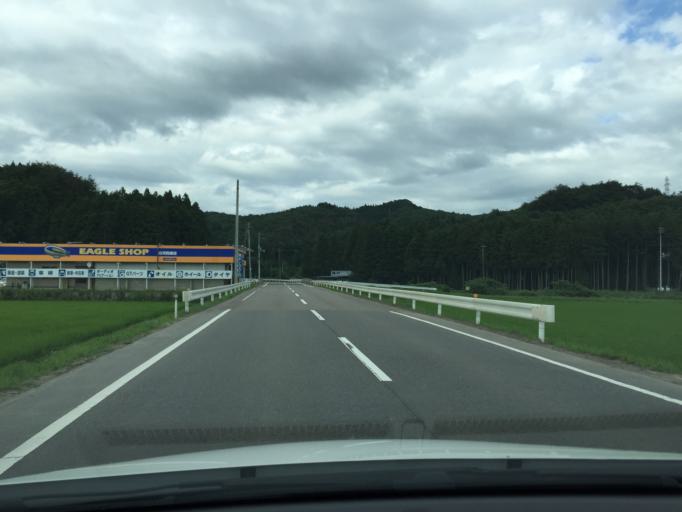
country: JP
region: Tochigi
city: Kuroiso
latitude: 37.1704
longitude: 140.1715
